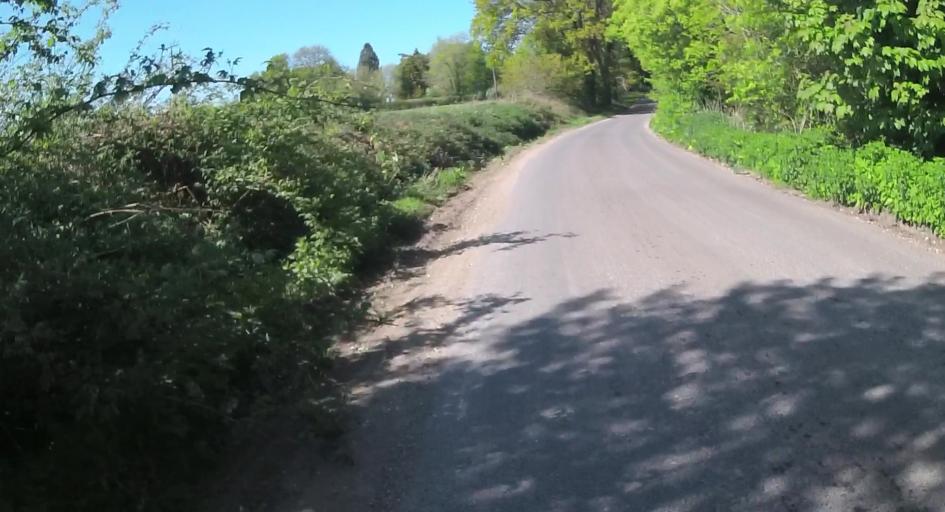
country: GB
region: England
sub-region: Hampshire
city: Alton
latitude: 51.1815
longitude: -1.0033
